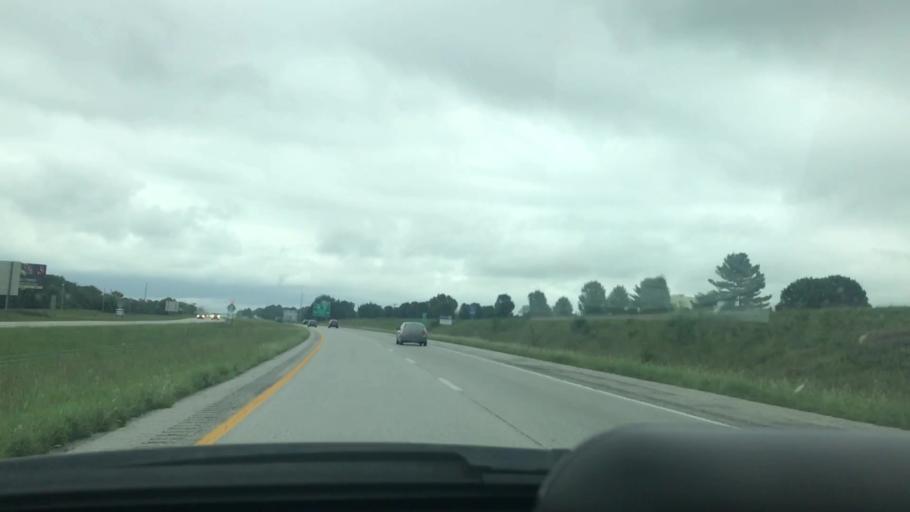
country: US
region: Missouri
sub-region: Jasper County
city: Duquesne
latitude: 37.0472
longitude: -94.4693
